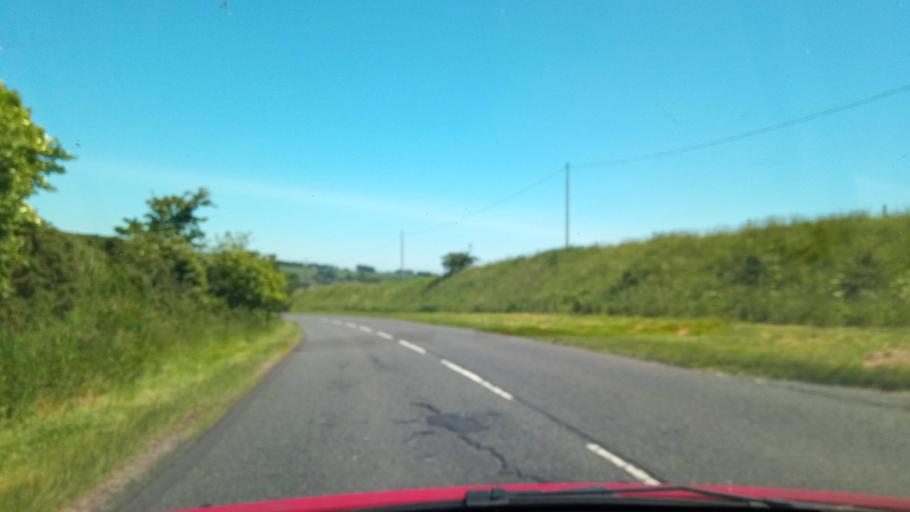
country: GB
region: Scotland
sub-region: The Scottish Borders
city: Kelso
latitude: 55.7015
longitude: -2.4659
